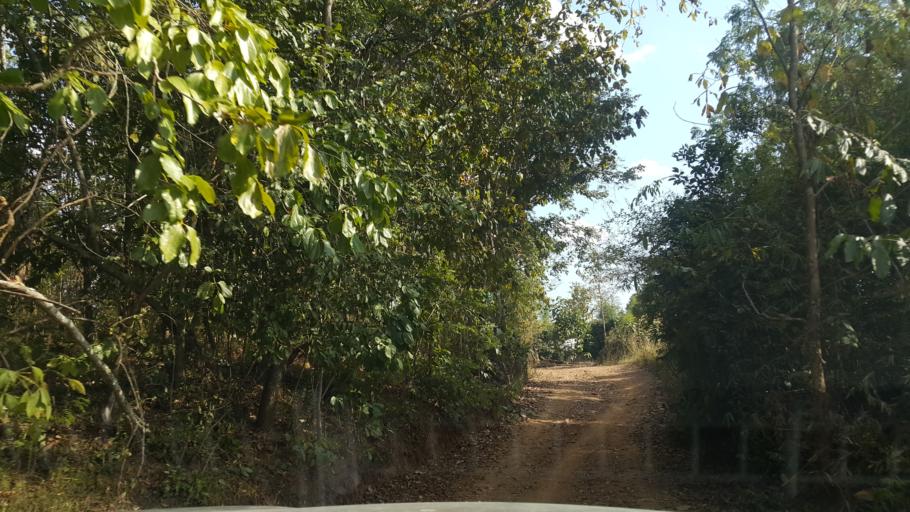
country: TH
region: Lamphun
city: Mae Tha
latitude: 18.5309
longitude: 99.1059
